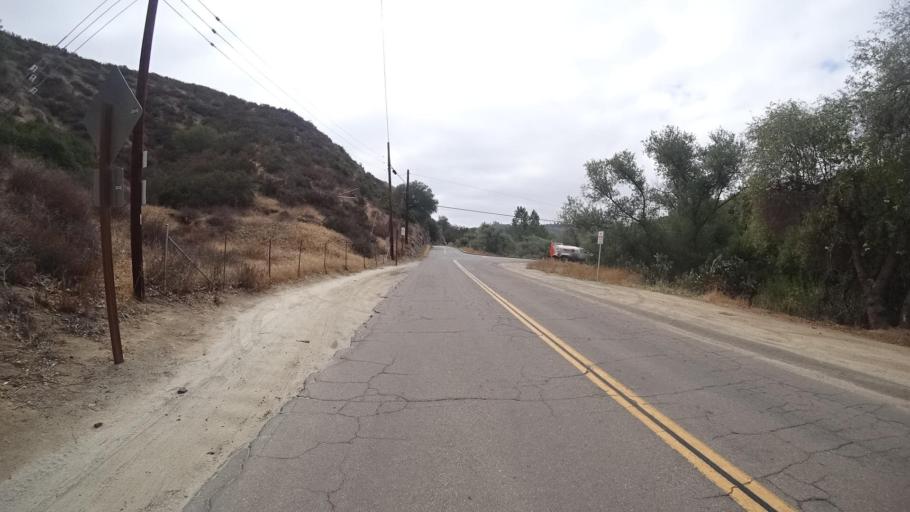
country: US
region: California
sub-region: San Diego County
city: Fallbrook
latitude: 33.4151
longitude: -117.2408
